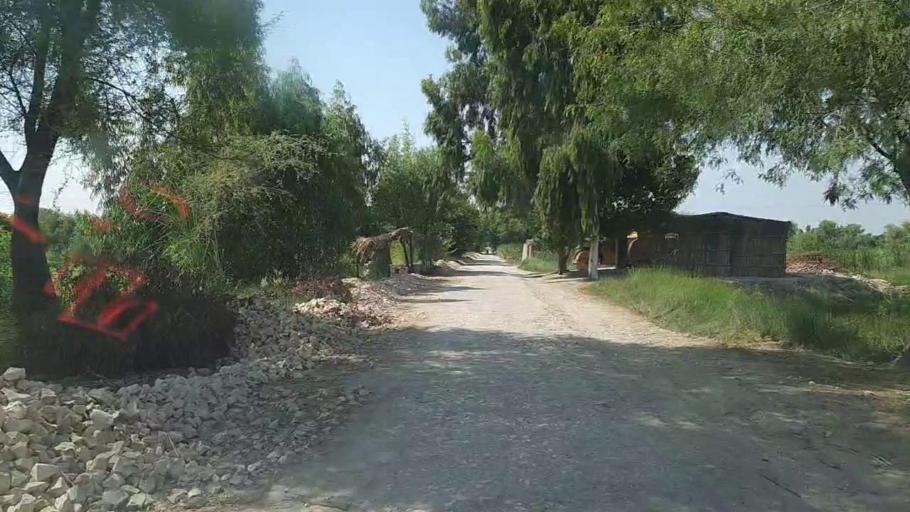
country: PK
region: Sindh
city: Khairpur
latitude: 28.0856
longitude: 69.6337
